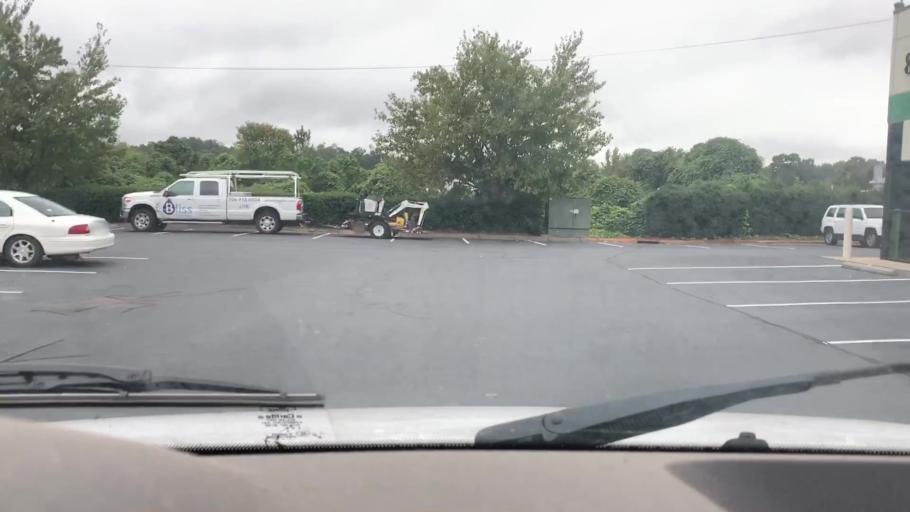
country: US
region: North Carolina
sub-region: Mecklenburg County
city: Huntersville
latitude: 35.3373
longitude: -80.8262
